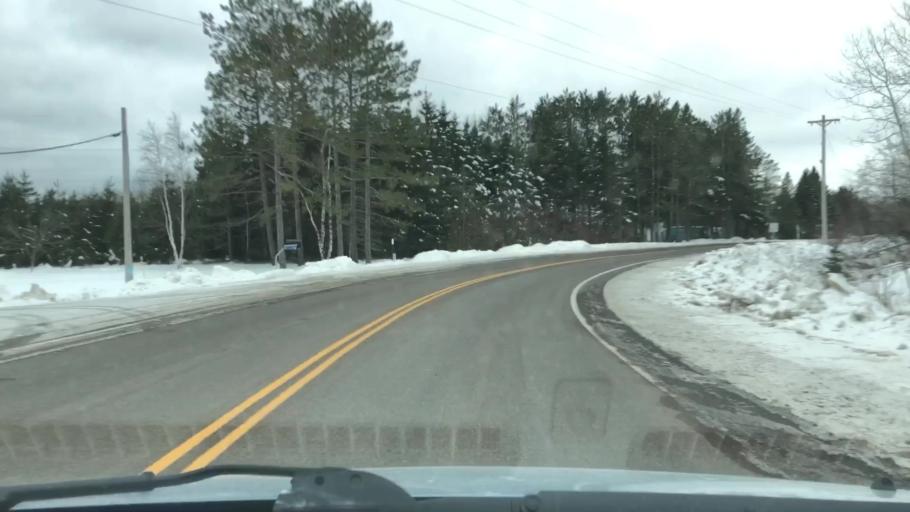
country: US
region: Minnesota
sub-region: Saint Louis County
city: Proctor
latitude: 46.6988
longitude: -92.2792
